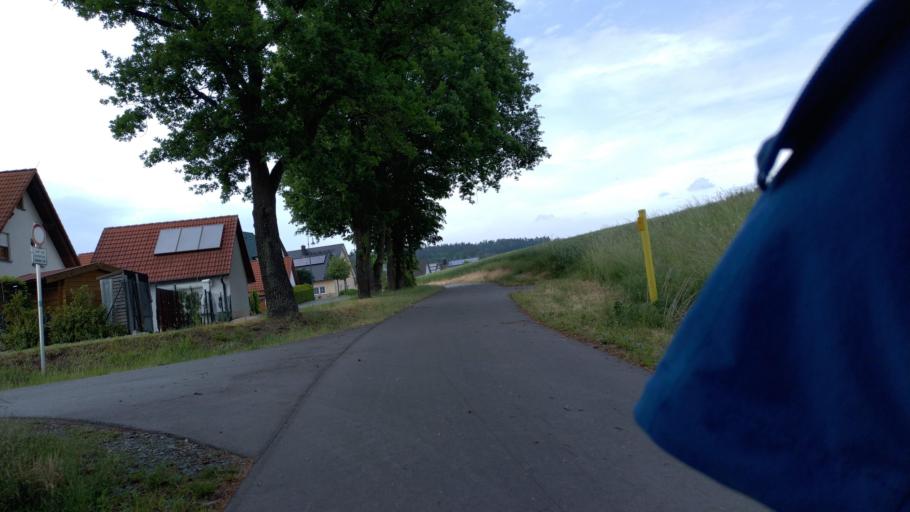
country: DE
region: Bavaria
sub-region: Upper Franconia
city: Harsdorf
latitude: 50.0234
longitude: 11.5748
